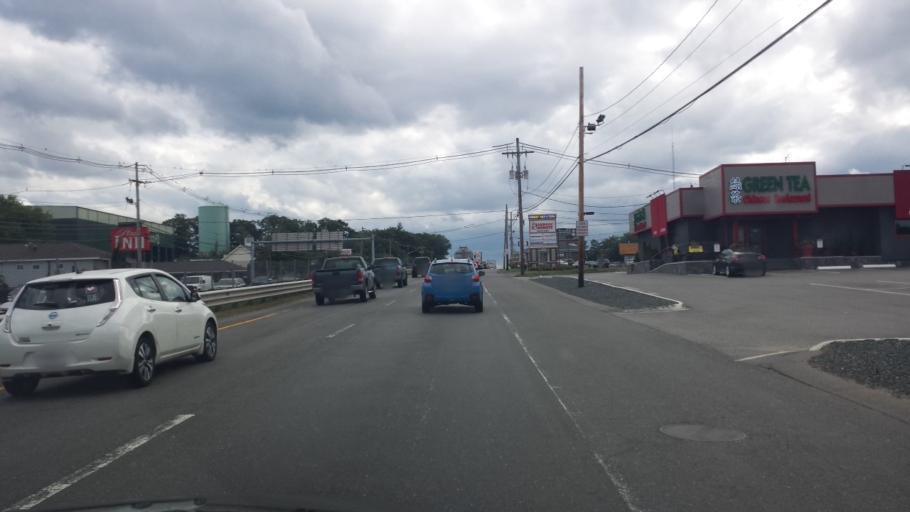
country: US
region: Massachusetts
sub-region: Essex County
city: South Peabody
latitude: 42.5351
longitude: -70.9898
